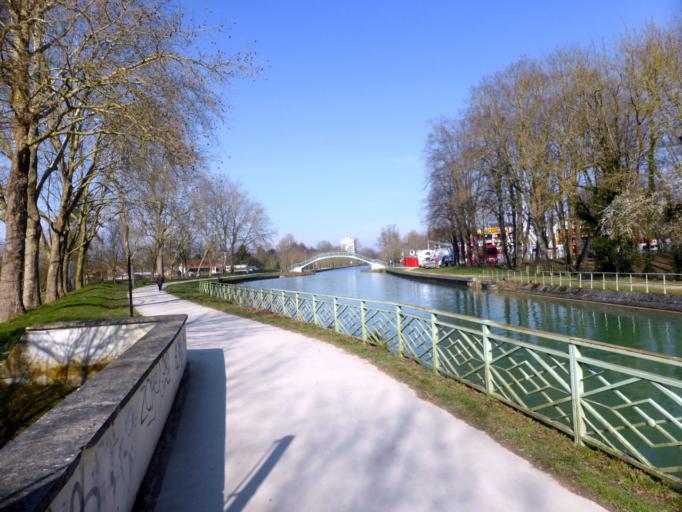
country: FR
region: Champagne-Ardenne
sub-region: Departement de la Marne
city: Chalons-en-Champagne
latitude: 48.9495
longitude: 4.3583
